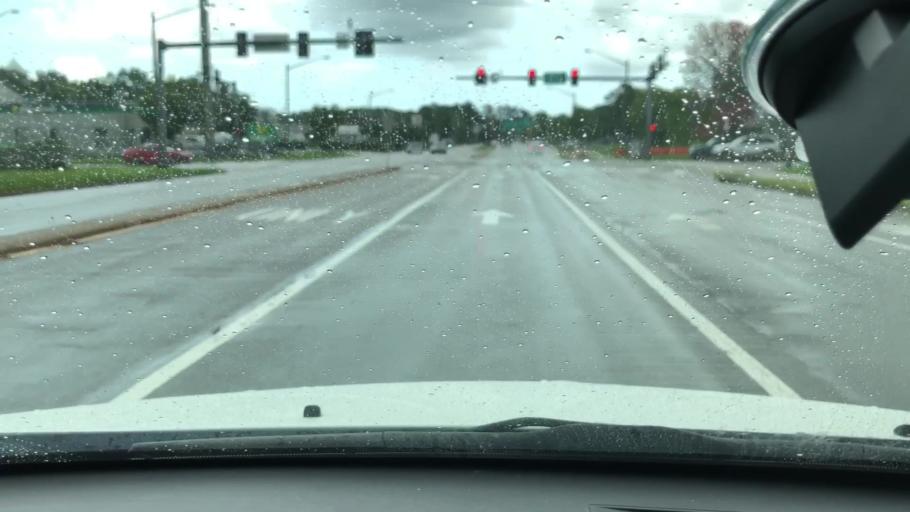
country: US
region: Virginia
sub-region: City of Chesapeake
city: Chesapeake
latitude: 36.8278
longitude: -76.1428
